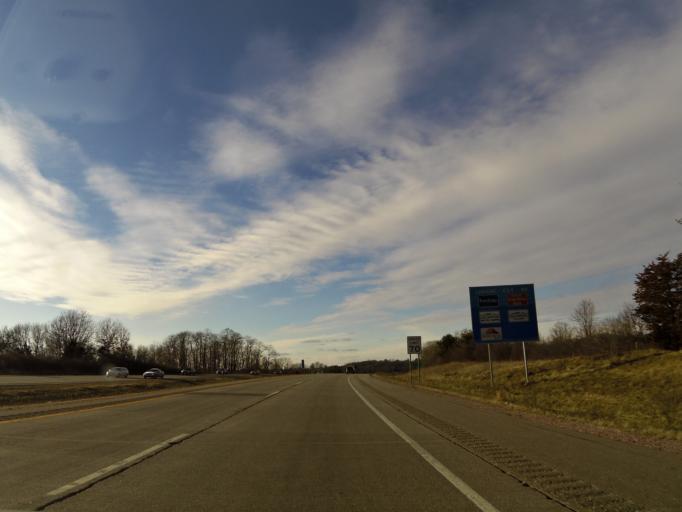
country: US
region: Wisconsin
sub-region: Sauk County
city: Lake Delton
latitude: 43.5714
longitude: -89.7928
